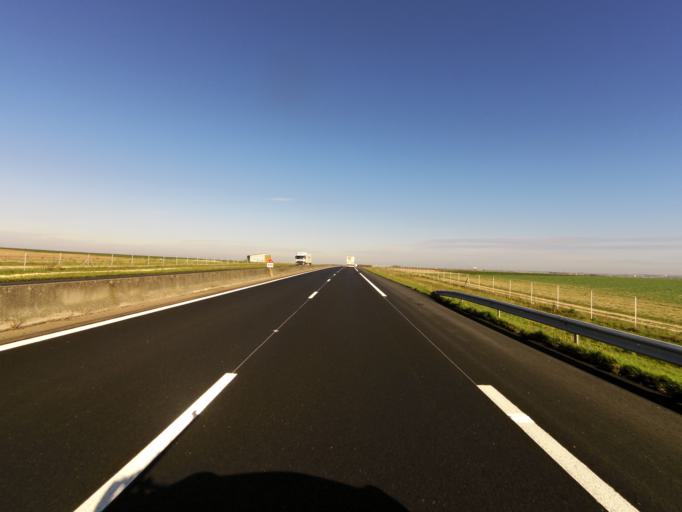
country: FR
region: Champagne-Ardenne
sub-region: Departement de la Marne
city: Fagnieres
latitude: 48.9241
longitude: 4.2834
